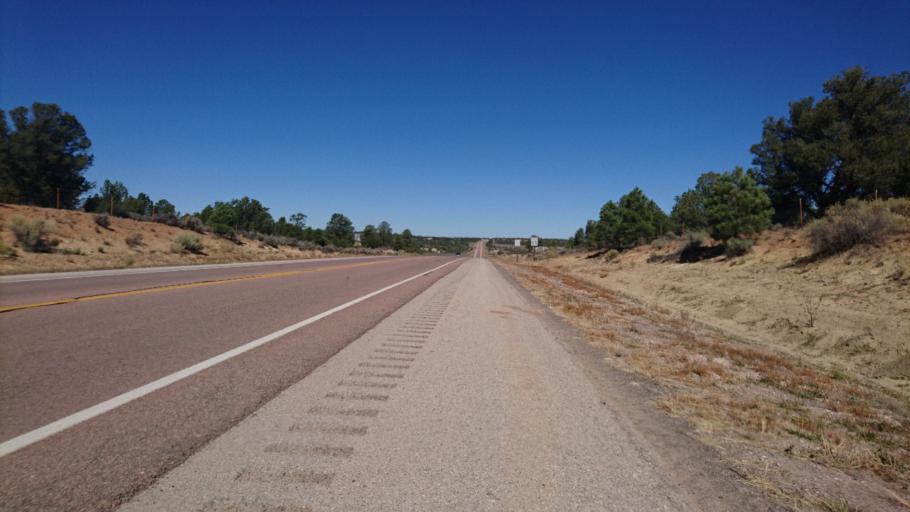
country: US
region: New Mexico
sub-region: McKinley County
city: Black Rock
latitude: 35.2842
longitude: -108.7557
